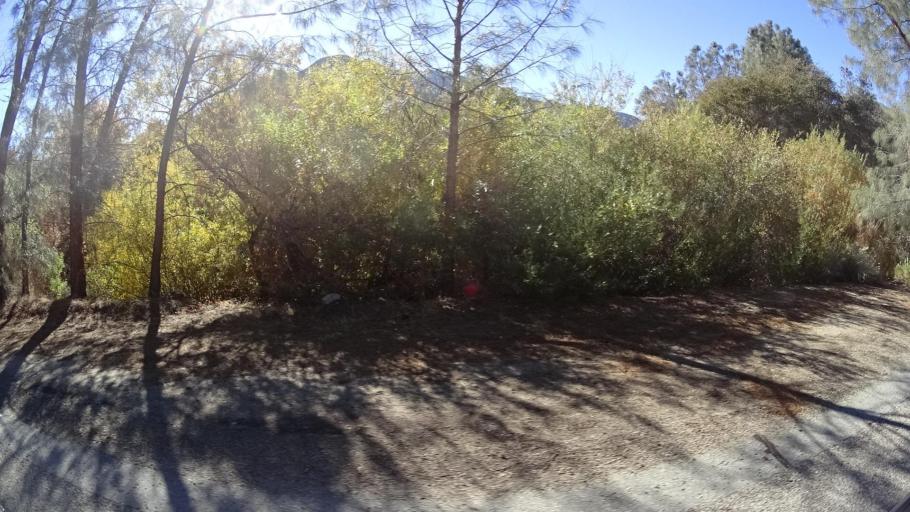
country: US
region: California
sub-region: Kern County
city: Kernville
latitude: 35.7817
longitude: -118.4408
